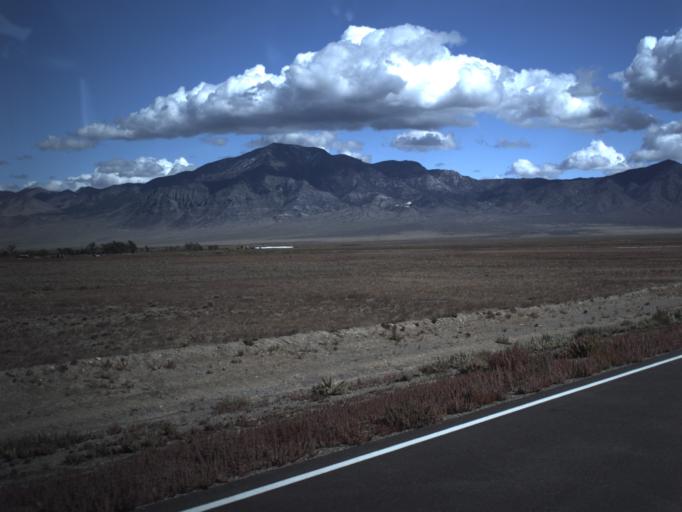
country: US
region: Utah
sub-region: Beaver County
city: Milford
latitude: 38.4803
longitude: -113.4370
